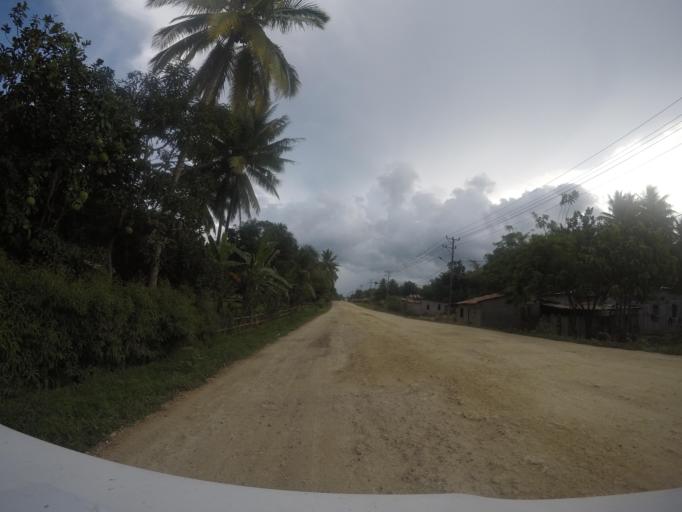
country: TL
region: Lautem
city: Lospalos
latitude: -8.5006
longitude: 126.9904
